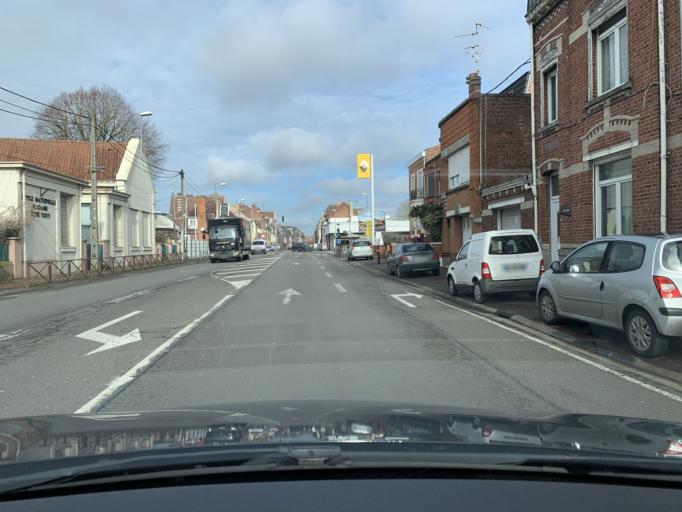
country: FR
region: Nord-Pas-de-Calais
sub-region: Departement du Nord
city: Douai
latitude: 50.3589
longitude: 3.0803
